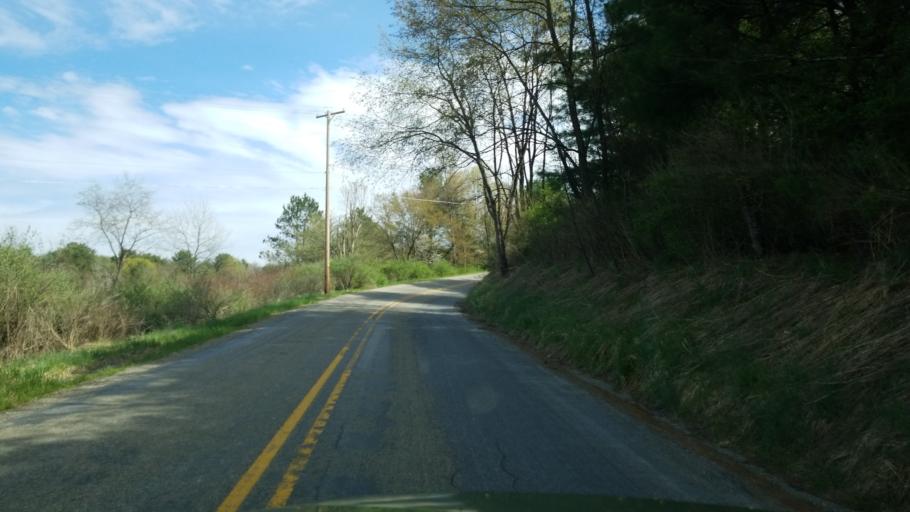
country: US
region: Pennsylvania
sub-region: Jefferson County
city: Brockway
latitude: 41.2310
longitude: -78.8512
